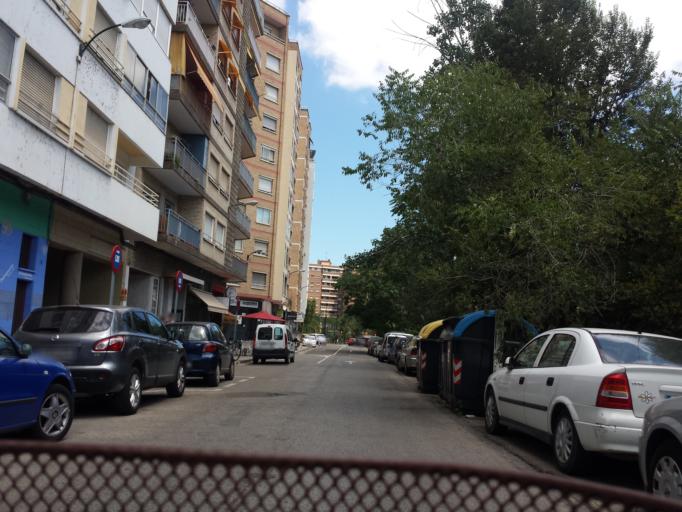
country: ES
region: Aragon
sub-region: Provincia de Zaragoza
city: Delicias
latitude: 41.6396
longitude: -0.8912
